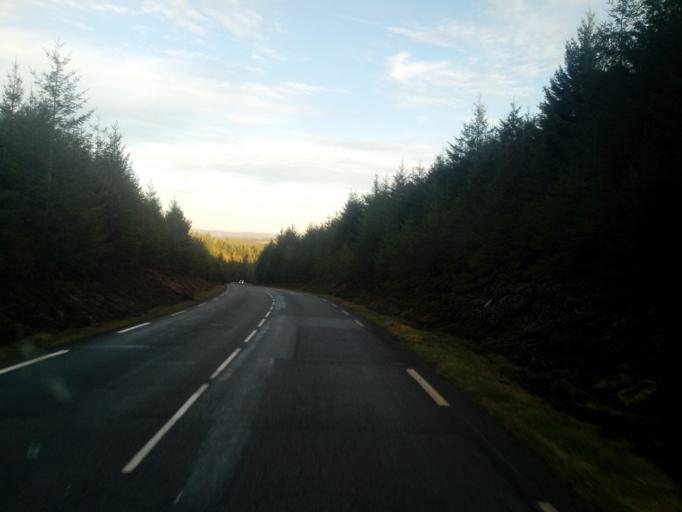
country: FR
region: Limousin
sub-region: Departement de la Correze
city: Meymac
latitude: 45.5780
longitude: 2.1111
